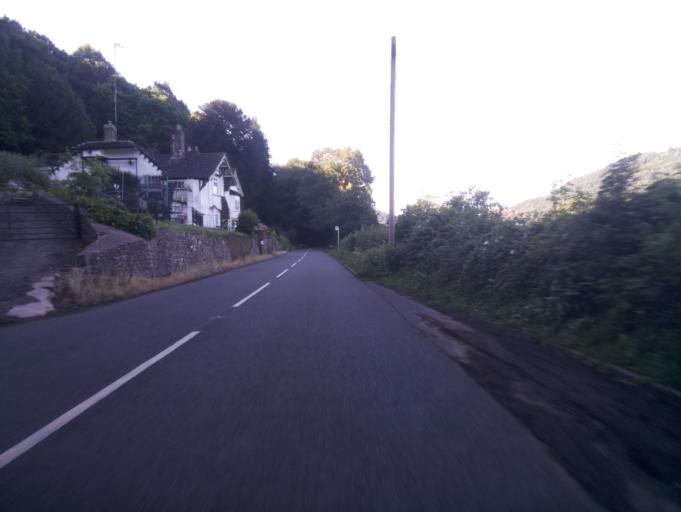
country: GB
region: Wales
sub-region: Monmouthshire
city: Tintern
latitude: 51.7536
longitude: -2.6621
